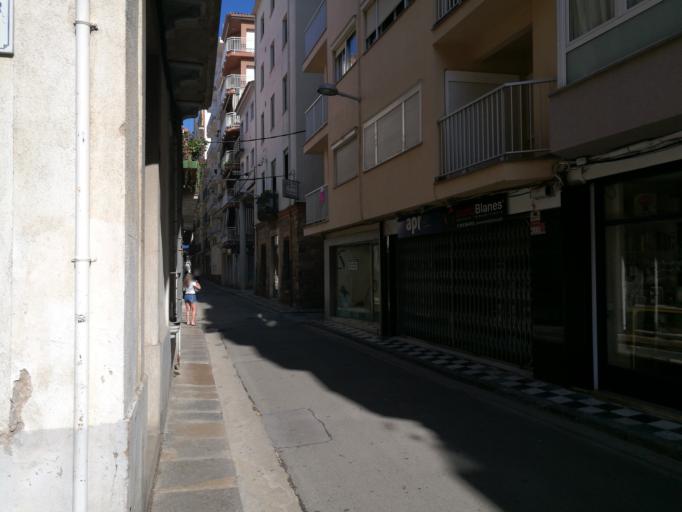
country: ES
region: Catalonia
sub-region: Provincia de Girona
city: Blanes
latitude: 41.6747
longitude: 2.7932
